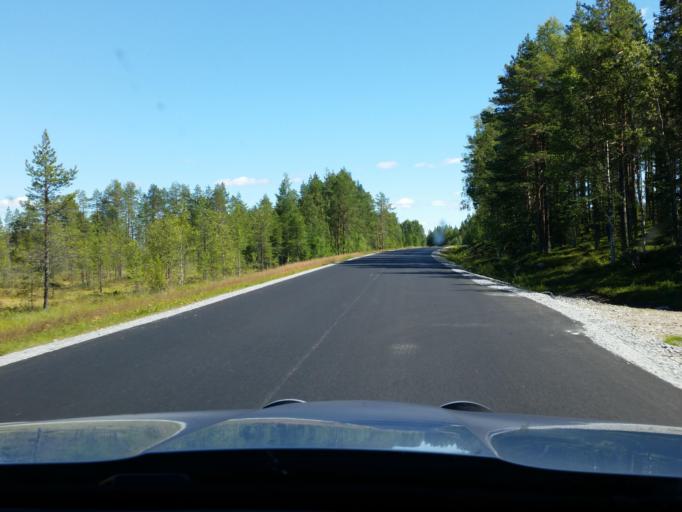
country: SE
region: Norrbotten
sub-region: Pitea Kommun
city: Roknas
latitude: 65.3421
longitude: 20.9761
